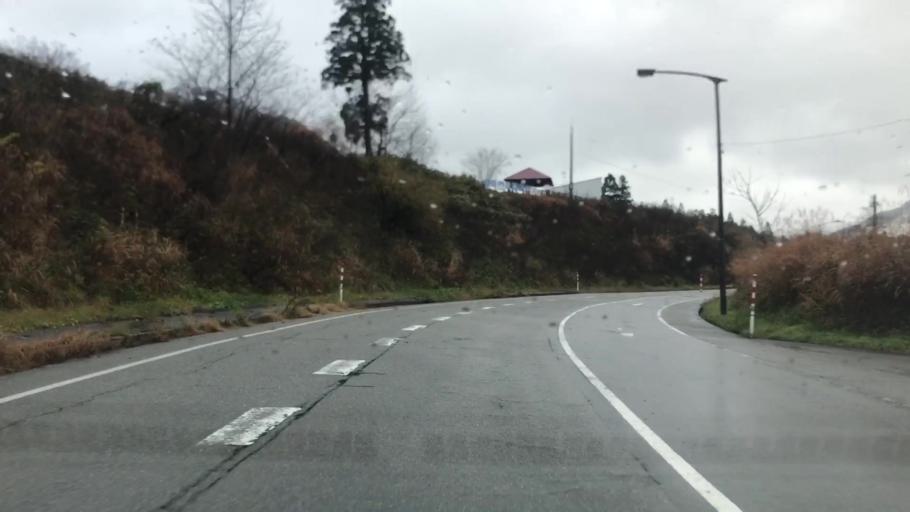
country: JP
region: Toyama
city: Kamiichi
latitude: 36.5777
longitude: 137.4134
